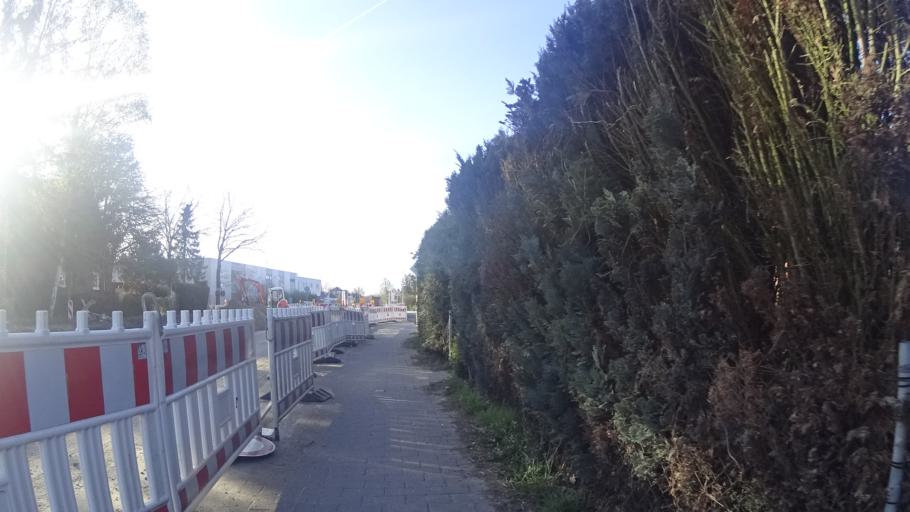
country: DE
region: North Rhine-Westphalia
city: Emsdetten
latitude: 52.1340
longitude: 7.5452
